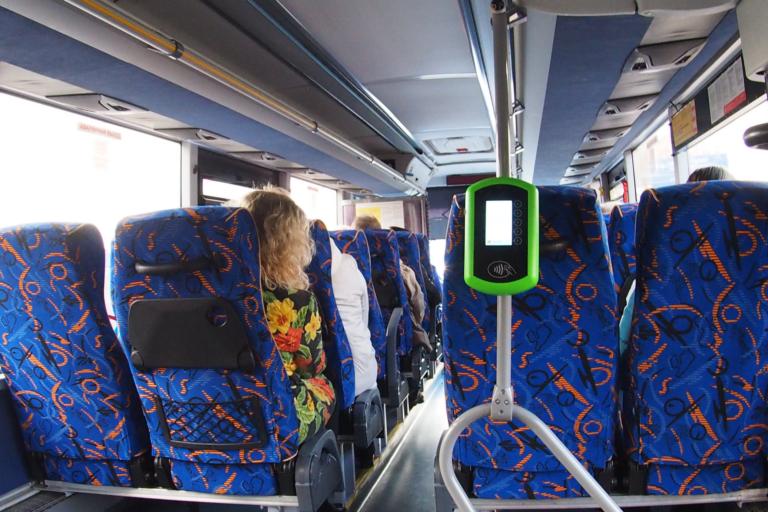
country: RU
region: Moskovskaya
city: Lobnya
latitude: 55.9996
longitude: 37.4238
